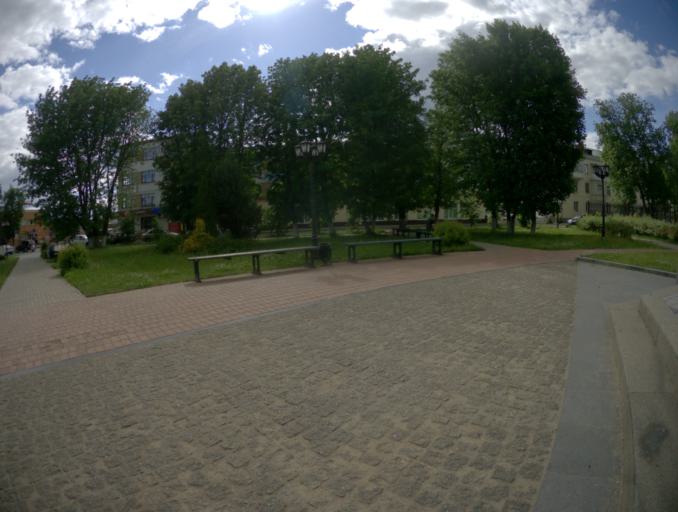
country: RU
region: Ivanovo
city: Shuya
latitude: 56.8560
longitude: 41.3840
